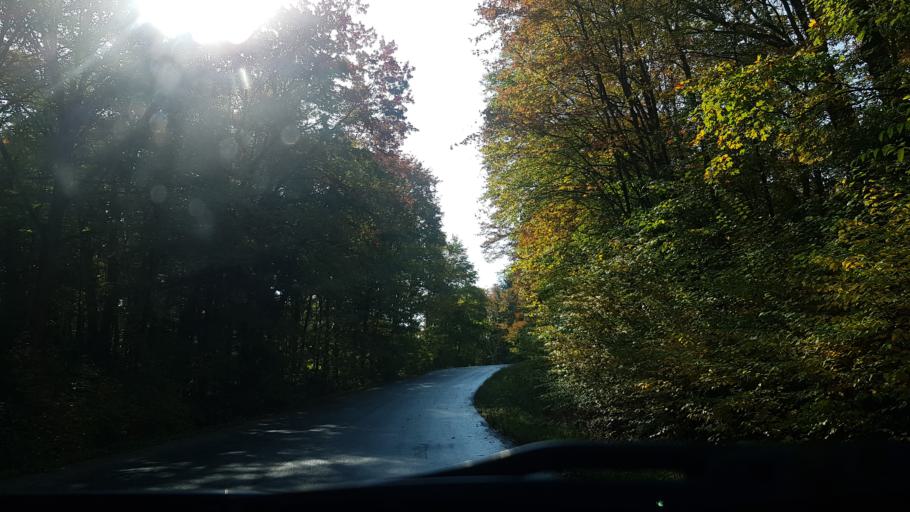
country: CA
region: Ontario
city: Bracebridge
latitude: 44.9560
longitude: -79.2462
